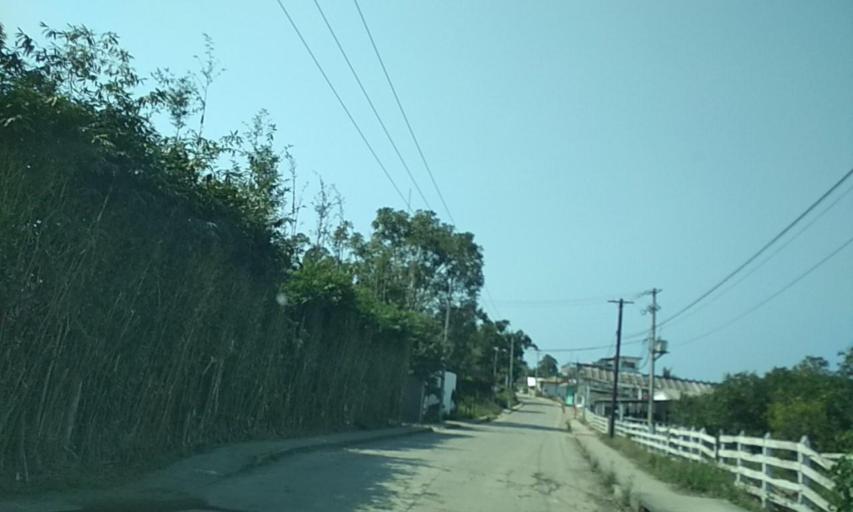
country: MX
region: Veracruz
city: Gutierrez Zamora
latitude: 20.4217
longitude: -97.1835
